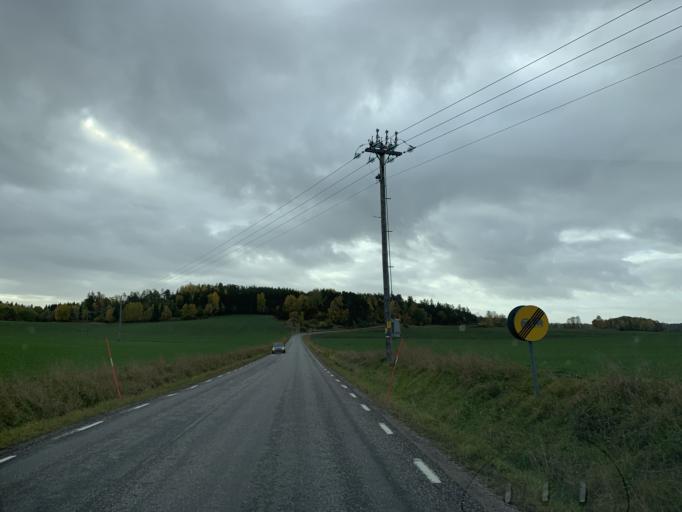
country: SE
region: Stockholm
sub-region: Nynashamns Kommun
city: Osmo
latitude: 58.9542
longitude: 17.7667
